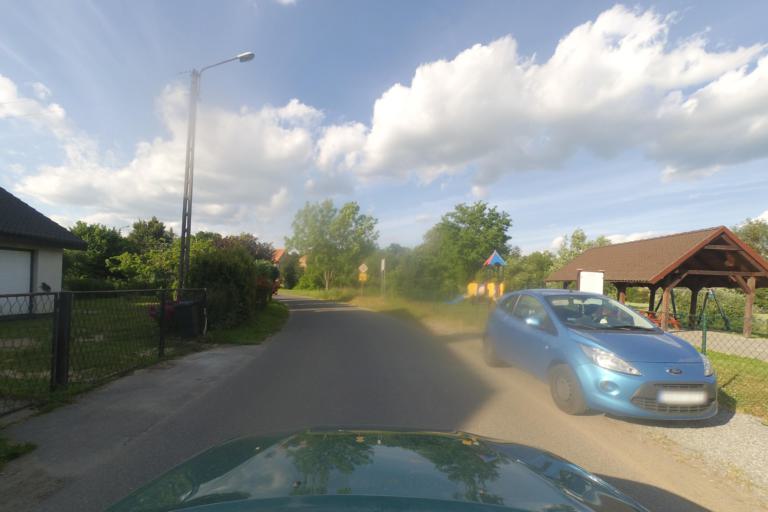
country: PL
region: Lower Silesian Voivodeship
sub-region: Powiat dzierzoniowski
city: Niemcza
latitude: 50.6936
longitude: 16.8512
